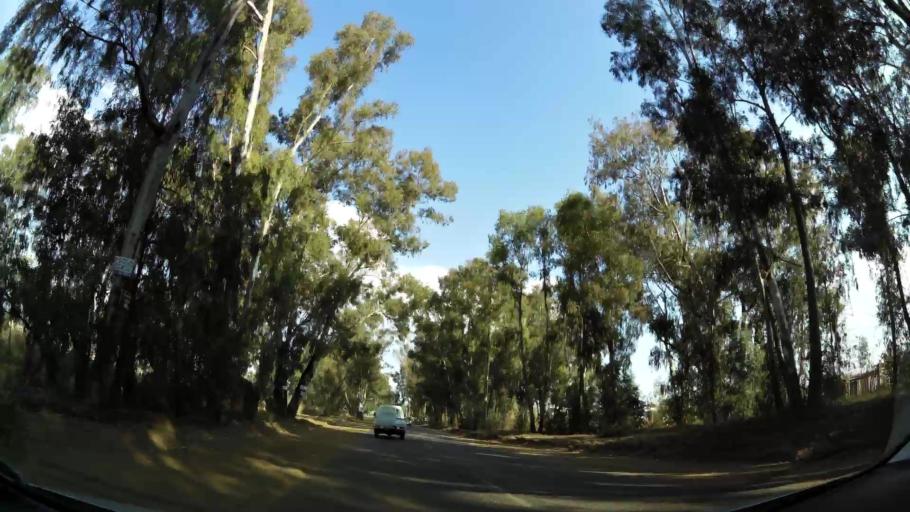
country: ZA
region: Gauteng
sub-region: Ekurhuleni Metropolitan Municipality
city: Tembisa
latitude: -25.9394
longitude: 28.2329
